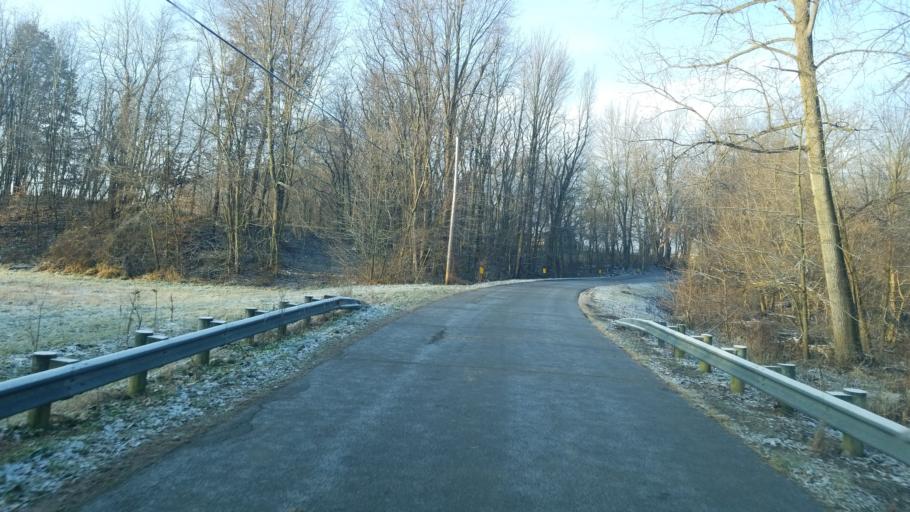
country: US
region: Ohio
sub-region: Crawford County
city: Galion
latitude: 40.7592
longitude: -82.8780
